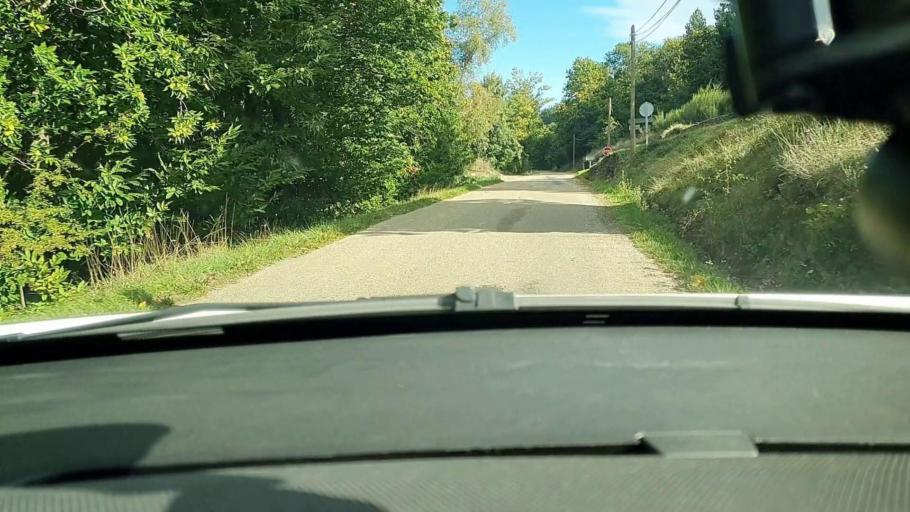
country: FR
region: Rhone-Alpes
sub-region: Departement de l'Ardeche
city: Les Vans
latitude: 44.4180
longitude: 4.0212
